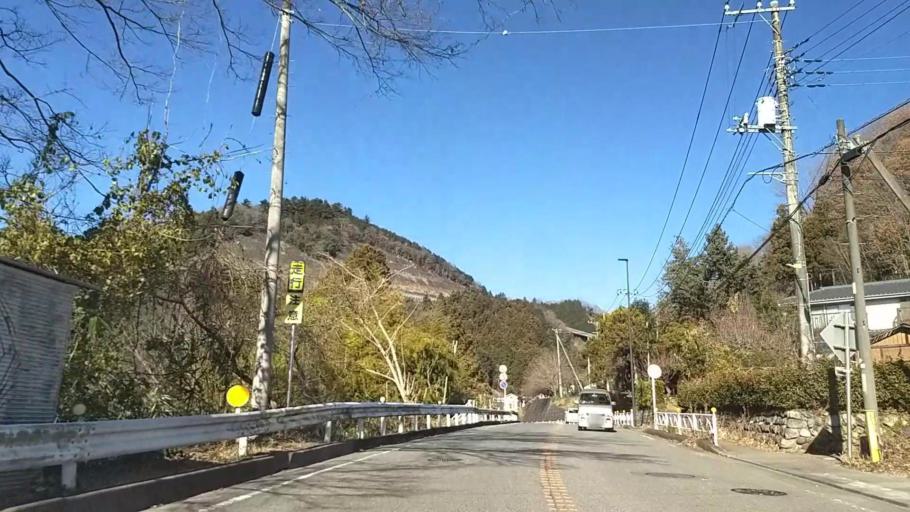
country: JP
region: Yamanashi
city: Uenohara
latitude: 35.6223
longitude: 139.2040
